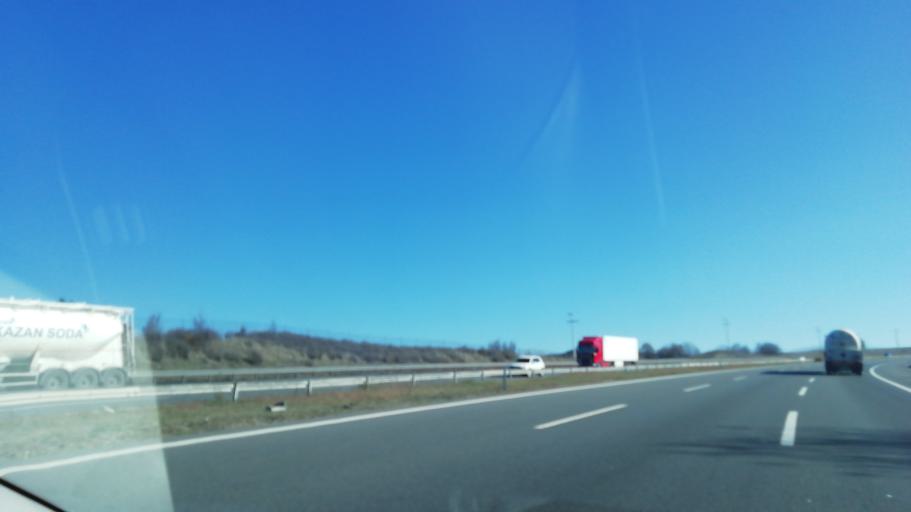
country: TR
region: Bolu
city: Yenicaga
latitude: 40.7644
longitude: 32.0552
